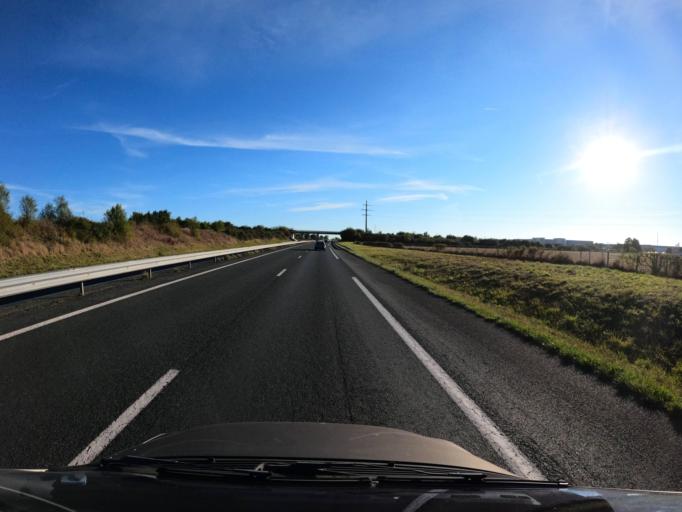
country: FR
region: Pays de la Loire
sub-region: Departement de Maine-et-Loire
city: Mazieres-en-Mauges
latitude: 47.0662
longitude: -0.8270
